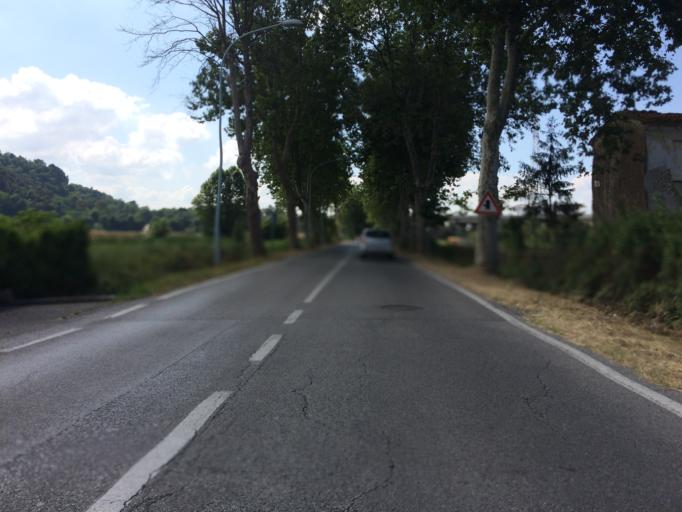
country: IT
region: Tuscany
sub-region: Provincia di Lucca
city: Piano di Conca
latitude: 43.8894
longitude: 10.2948
